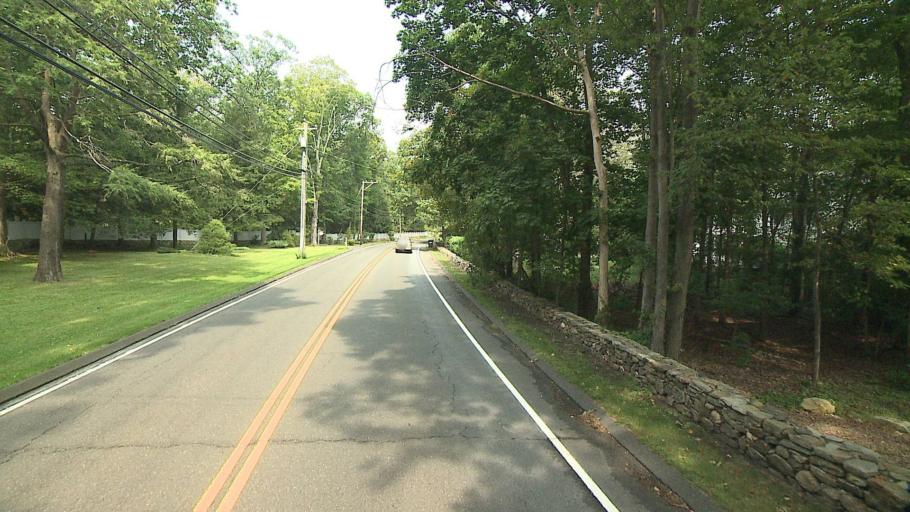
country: US
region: Connecticut
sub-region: Fairfield County
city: Ridgefield
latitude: 41.2704
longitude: -73.4806
